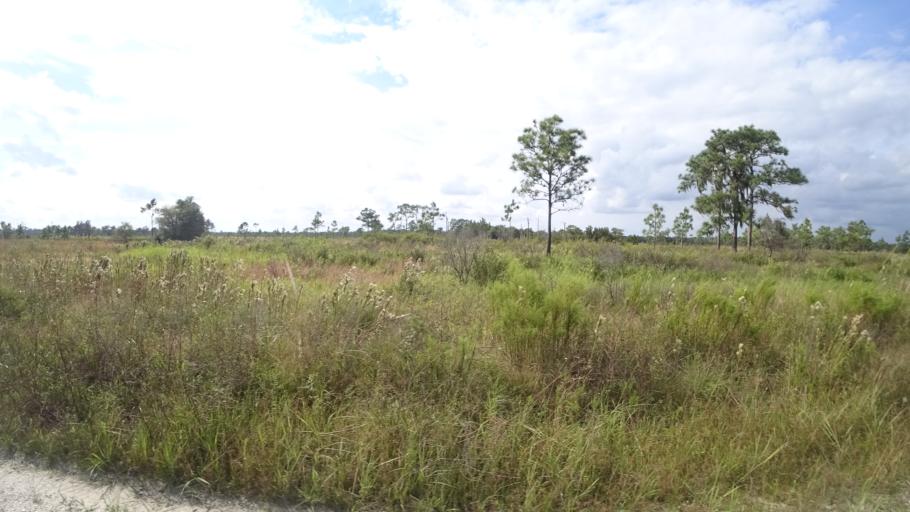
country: US
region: Florida
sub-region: Hillsborough County
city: Wimauma
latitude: 27.5372
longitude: -82.1291
